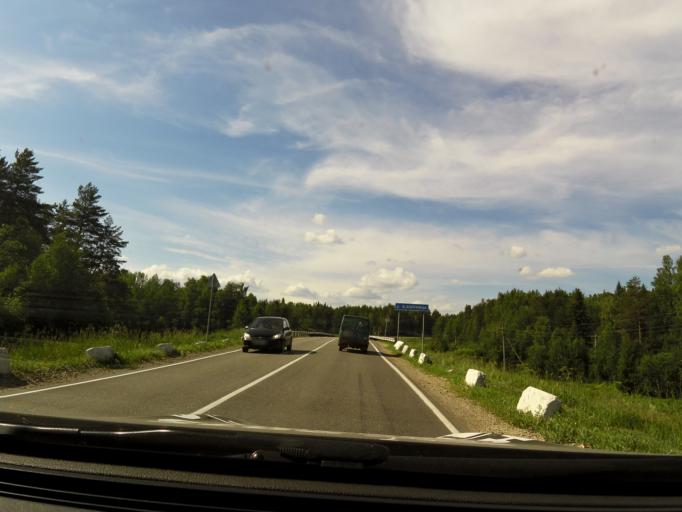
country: RU
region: Kirov
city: Belaya Kholunitsa
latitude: 58.8355
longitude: 50.6895
